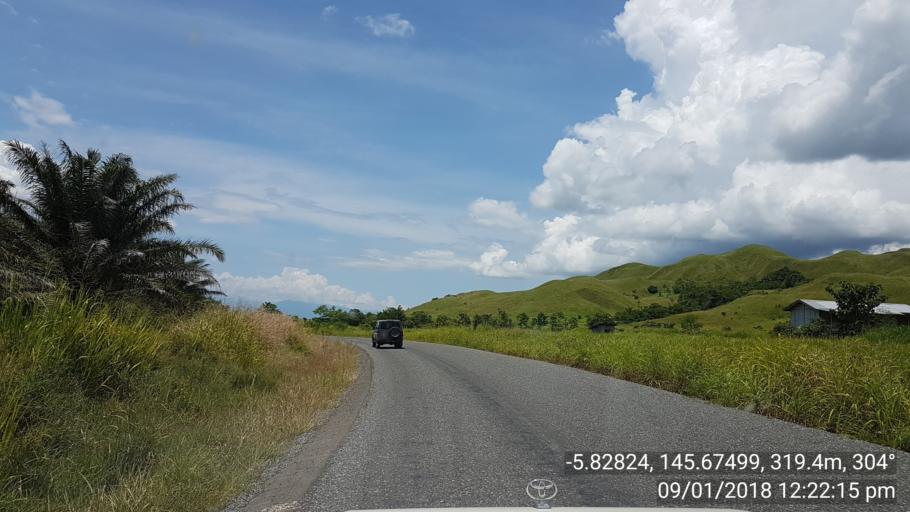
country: PG
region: Eastern Highlands
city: Goroka
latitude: -5.8288
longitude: 145.6754
